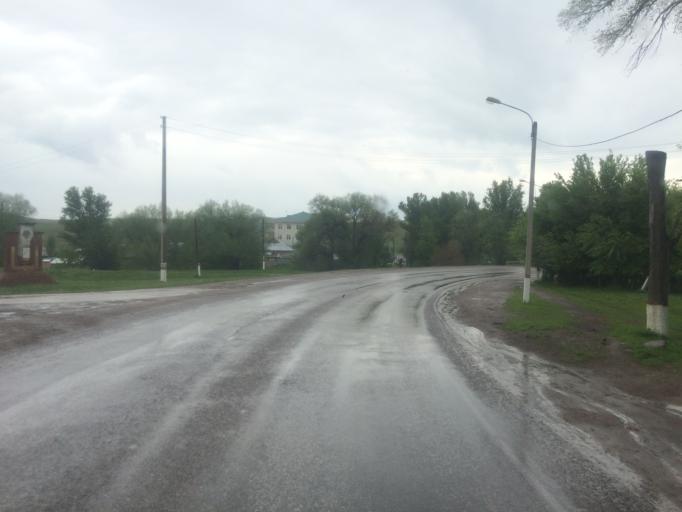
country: KZ
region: Zhambyl
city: Georgiyevka
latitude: 43.2346
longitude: 74.7591
